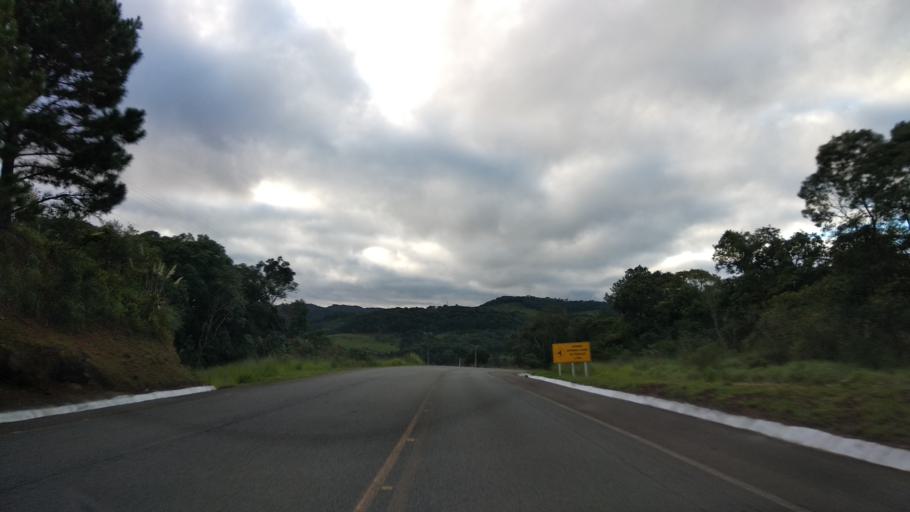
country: BR
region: Santa Catarina
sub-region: Campos Novos
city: Campos Novos
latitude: -27.5344
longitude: -50.8715
